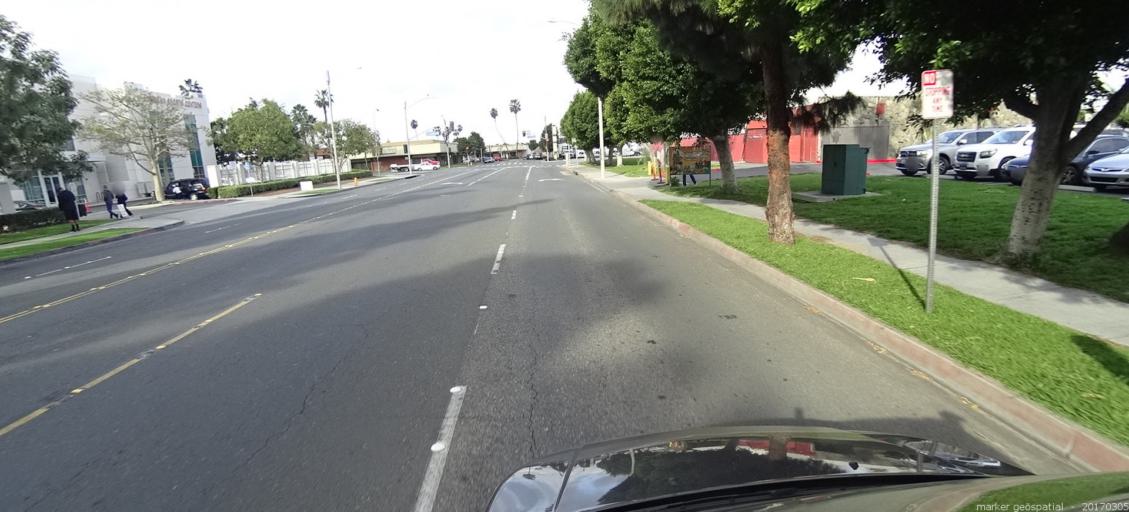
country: US
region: California
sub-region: Orange County
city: Anaheim
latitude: 33.8107
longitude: -117.9049
